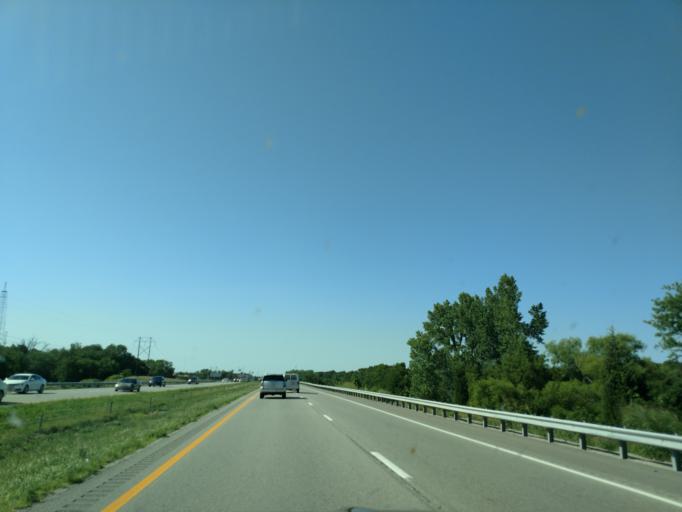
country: US
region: Missouri
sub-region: Buchanan County
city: Saint Joseph
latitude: 39.7610
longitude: -94.7913
